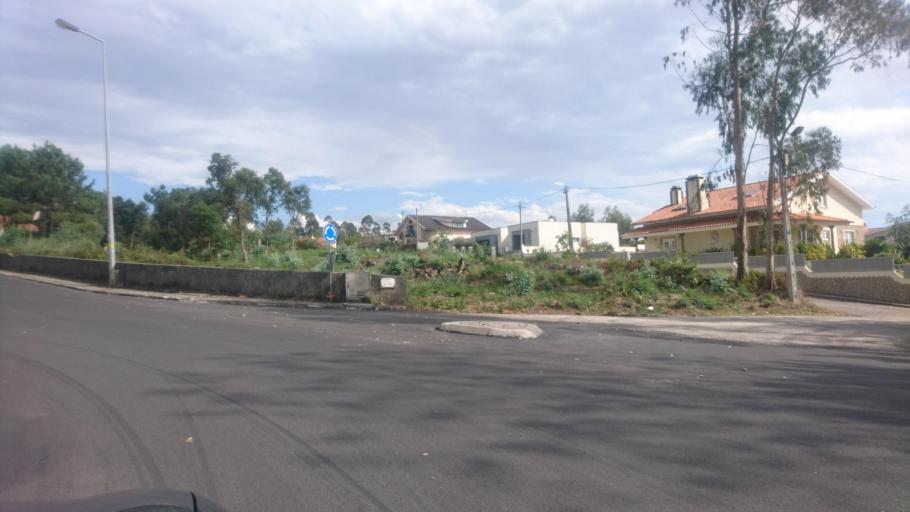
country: PT
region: Aveiro
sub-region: Ovar
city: Cortegaca
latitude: 40.9490
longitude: -8.6065
